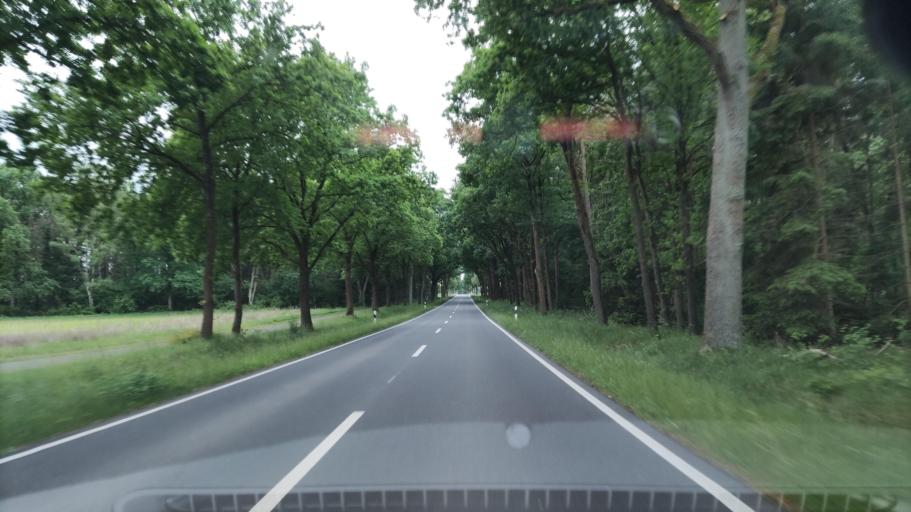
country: DE
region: Lower Saxony
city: Fintel
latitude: 53.1061
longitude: 9.6871
